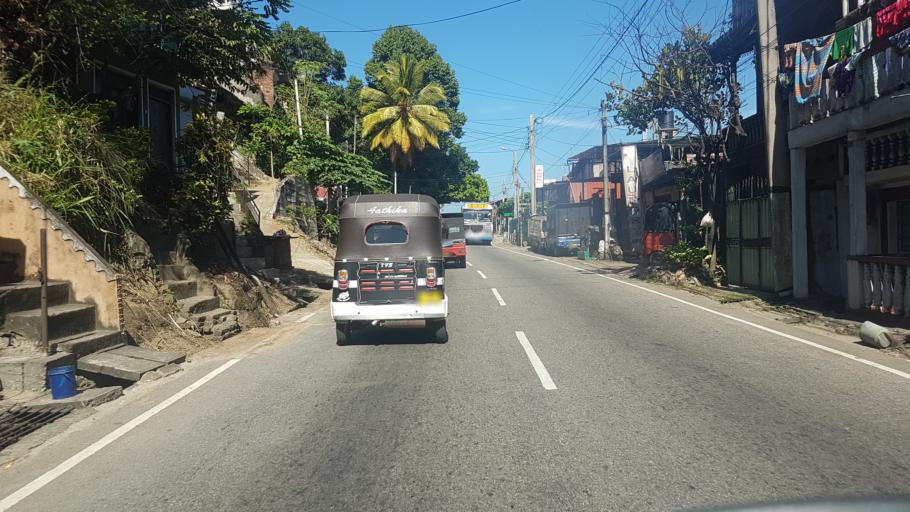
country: LK
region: Central
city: Kandy
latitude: 7.2883
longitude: 80.6575
